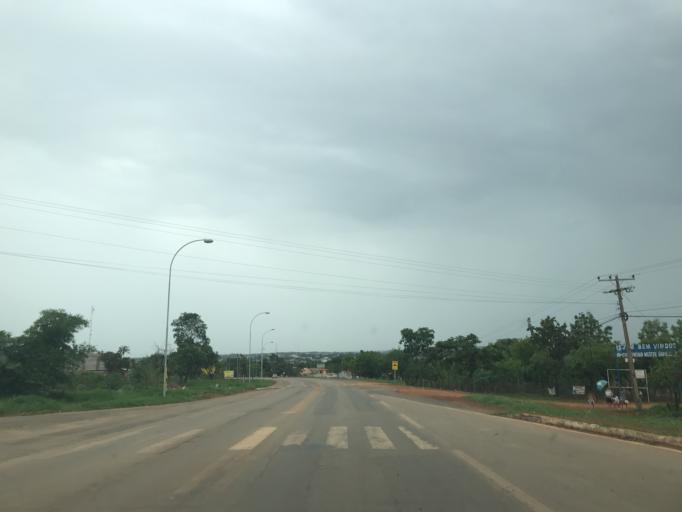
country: BR
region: Goias
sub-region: Planaltina
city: Planaltina
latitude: -15.6368
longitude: -47.6768
